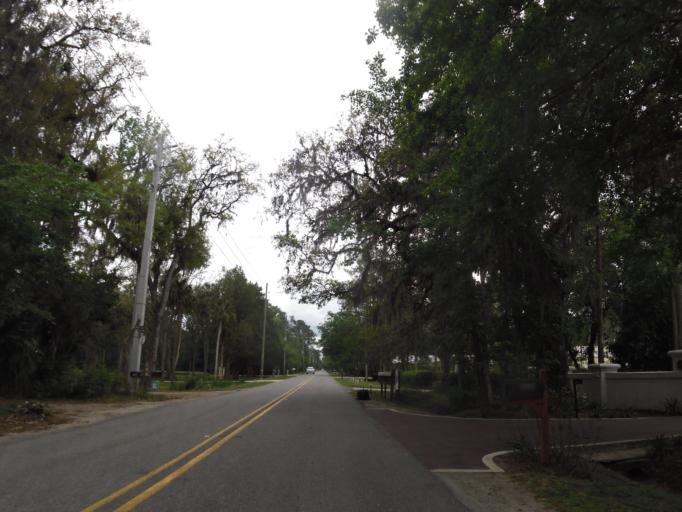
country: US
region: Florida
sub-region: Saint Johns County
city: Palm Valley
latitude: 30.1970
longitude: -81.4054
